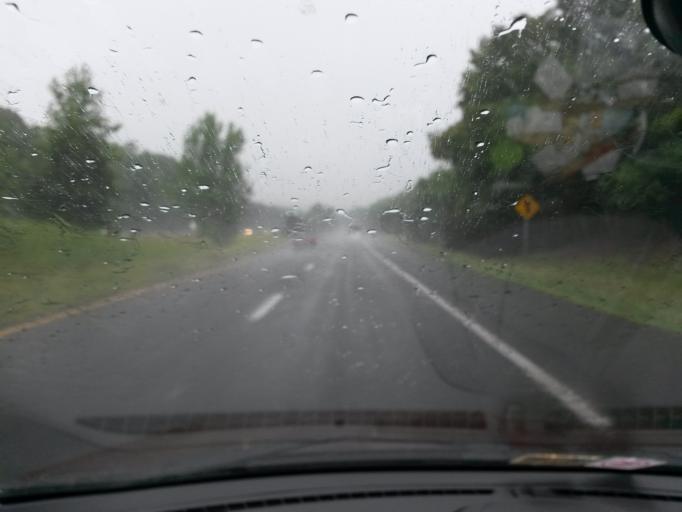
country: US
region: Virginia
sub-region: Louisa County
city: Louisa
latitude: 37.8431
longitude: -77.9811
